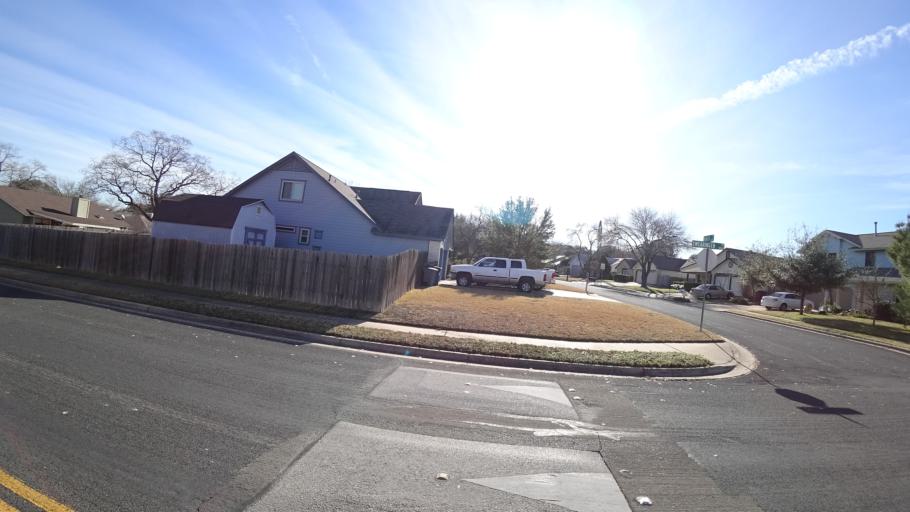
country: US
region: Texas
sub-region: Travis County
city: Wells Branch
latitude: 30.3892
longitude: -97.6974
